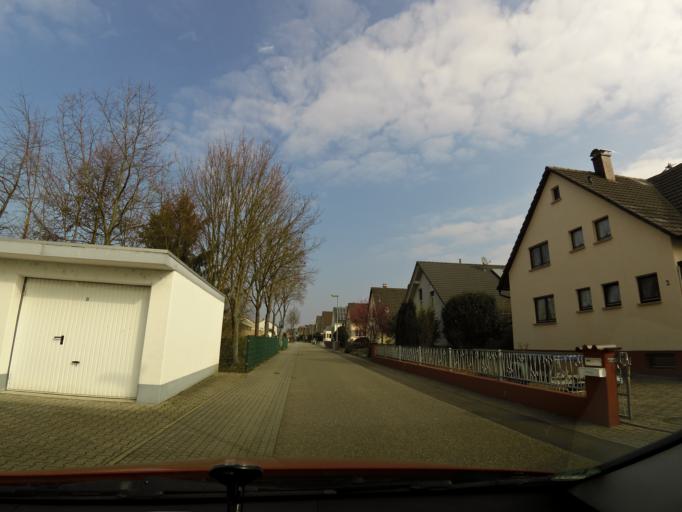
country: DE
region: Baden-Wuerttemberg
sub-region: Freiburg Region
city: Kehl
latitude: 48.5963
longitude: 7.8668
